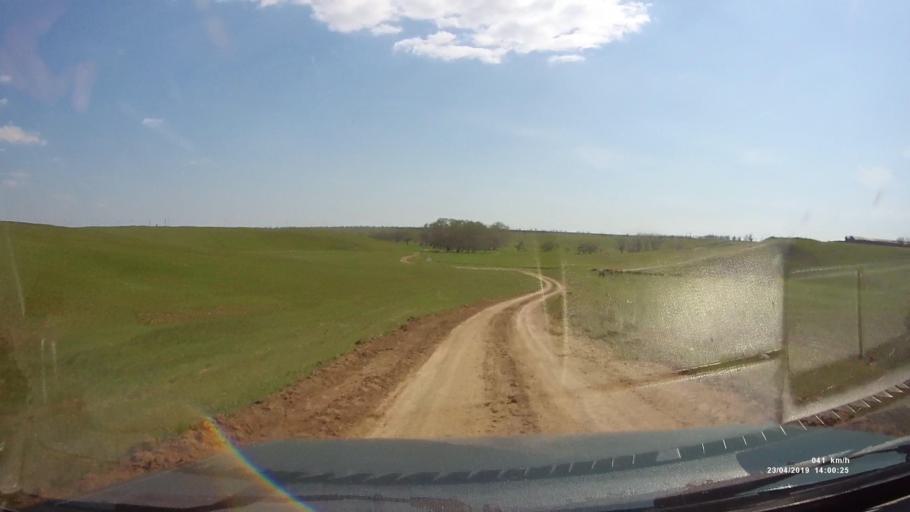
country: RU
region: Rostov
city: Remontnoye
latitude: 46.5597
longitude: 42.9469
